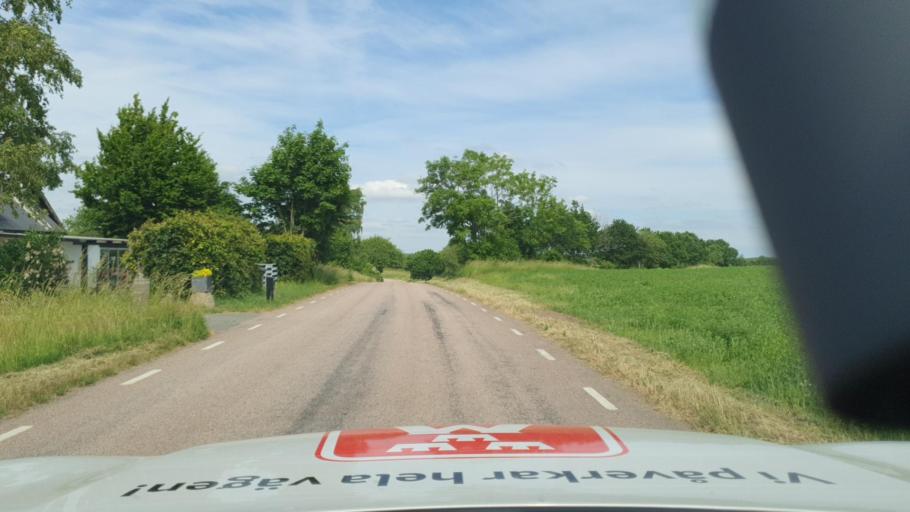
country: SE
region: Skane
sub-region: Sjobo Kommun
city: Sjoebo
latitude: 55.7162
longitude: 13.7912
